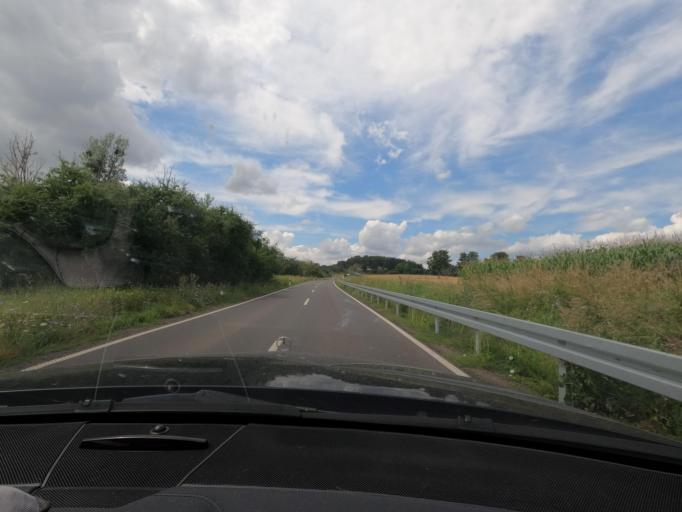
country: DE
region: Hesse
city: Hain-Grundau
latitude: 50.2108
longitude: 9.1213
